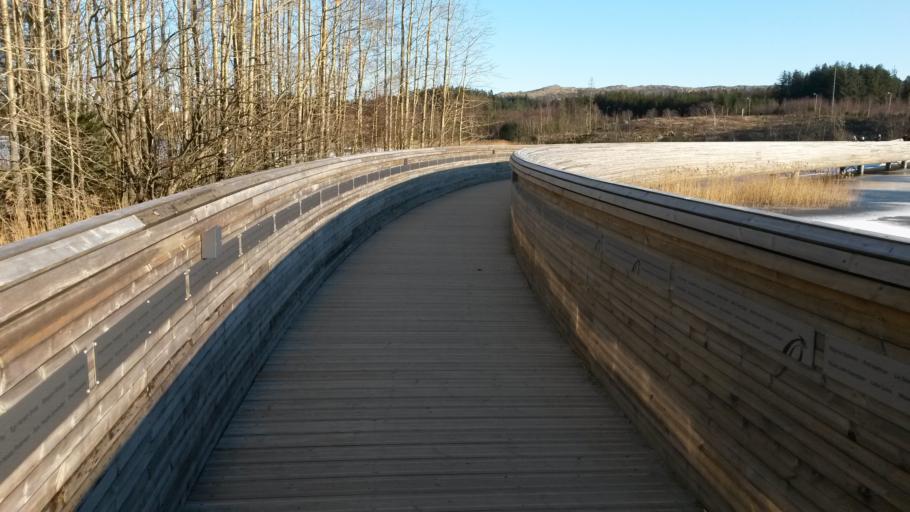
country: NO
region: Rogaland
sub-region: Time
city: Bryne
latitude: 58.7592
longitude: 5.6807
